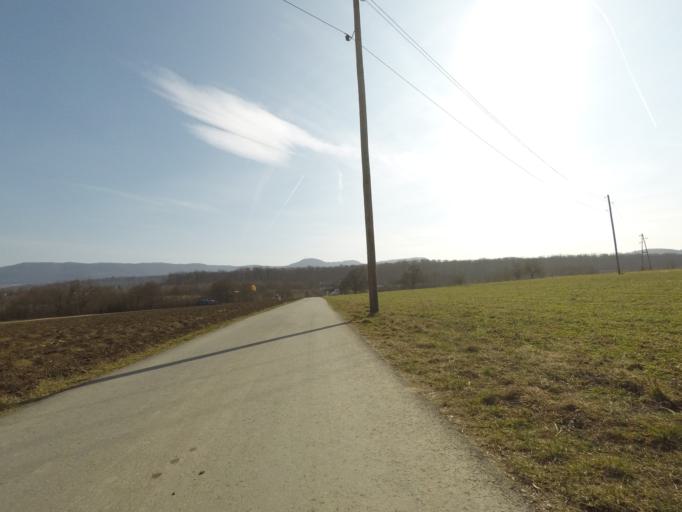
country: DE
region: Baden-Wuerttemberg
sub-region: Tuebingen Region
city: Metzingen
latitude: 48.5315
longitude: 9.2606
